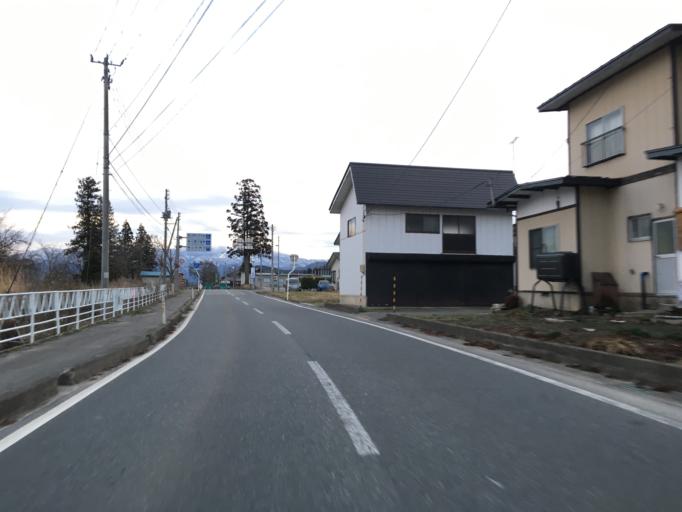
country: JP
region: Yamagata
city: Yonezawa
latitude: 37.9651
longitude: 140.0667
